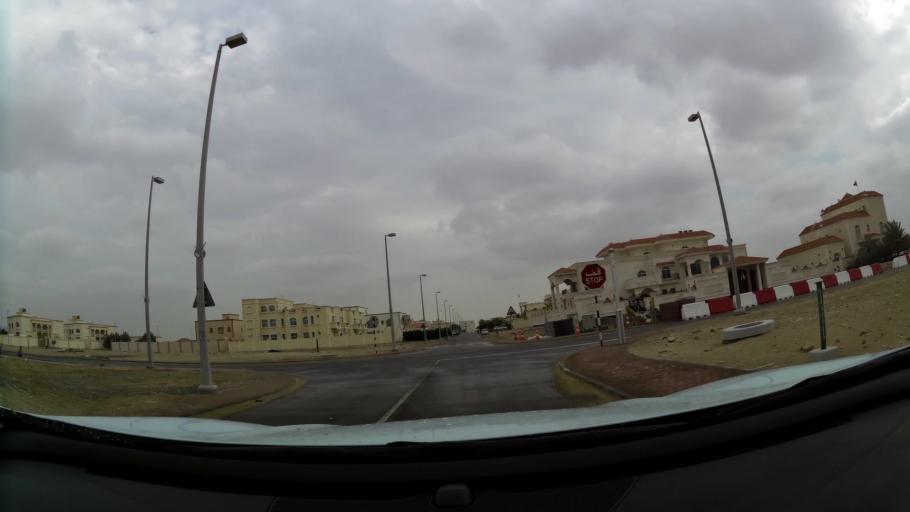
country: AE
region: Abu Dhabi
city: Abu Dhabi
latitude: 24.3552
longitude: 54.6189
